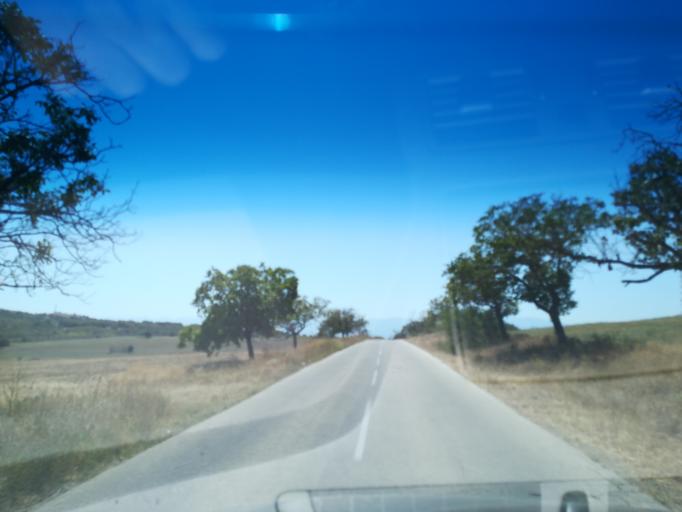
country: BG
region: Pazardzhik
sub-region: Obshtina Pazardzhik
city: Pazardzhik
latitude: 42.3166
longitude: 24.4059
